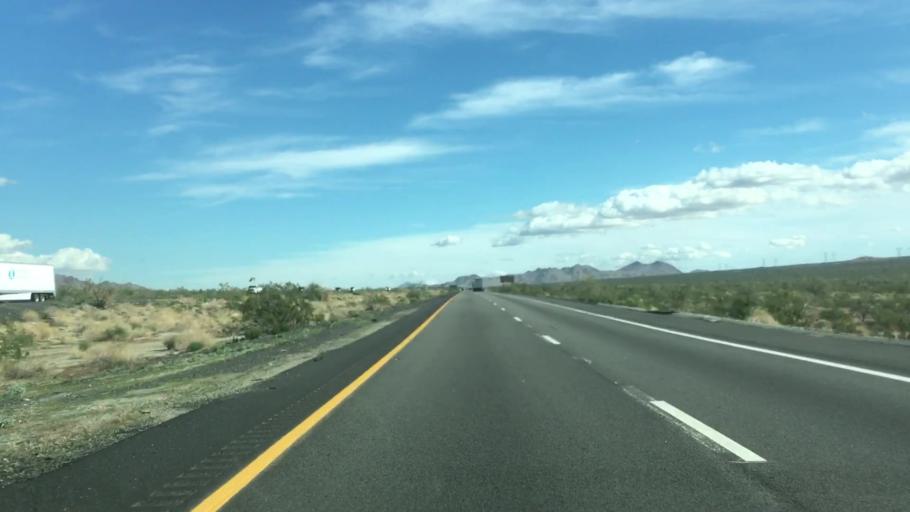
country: US
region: California
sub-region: Riverside County
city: Mecca
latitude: 33.6609
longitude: -115.8228
